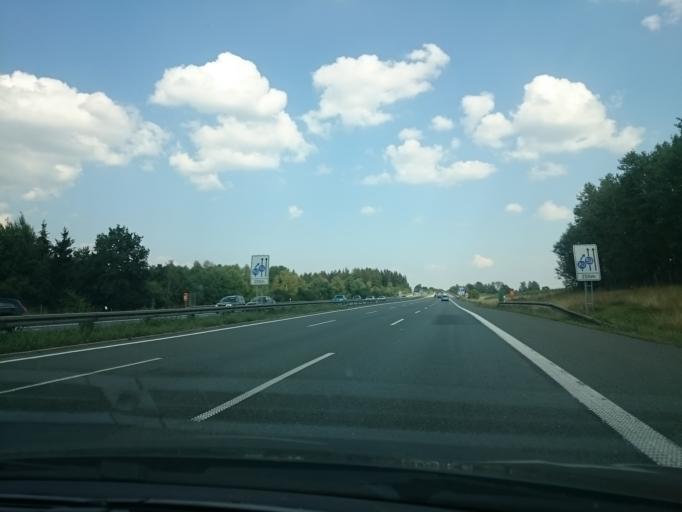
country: DE
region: Saxony
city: Neuensalz
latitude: 50.5320
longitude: 12.2486
